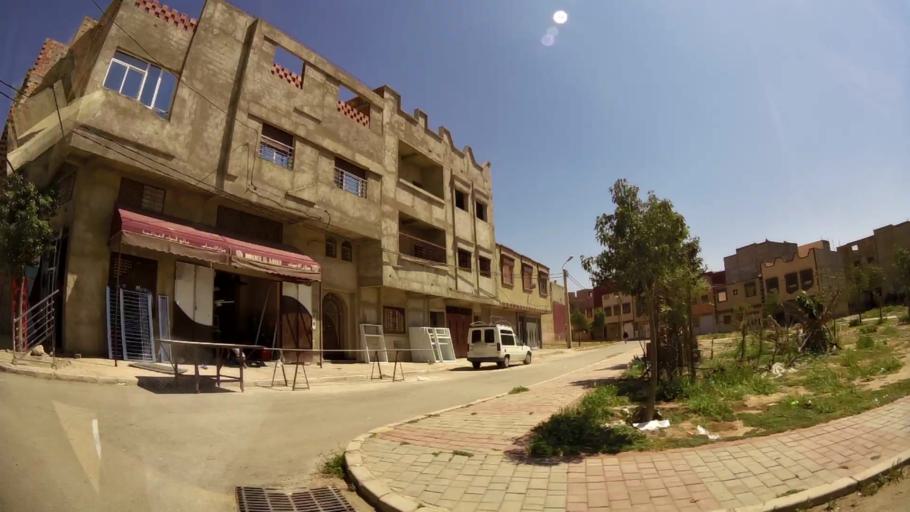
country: MA
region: Oriental
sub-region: Oujda-Angad
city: Oujda
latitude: 34.6892
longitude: -1.9343
